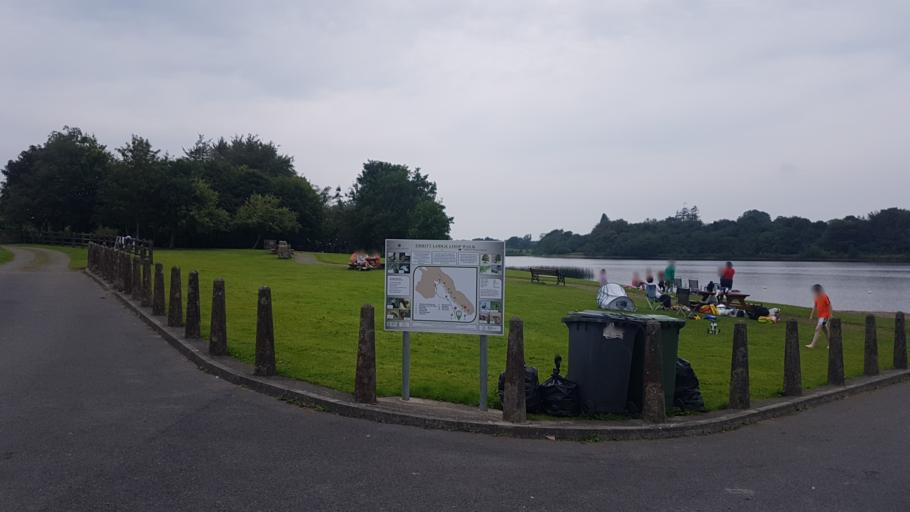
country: IE
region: Connaught
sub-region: Maigh Eo
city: Ballyhaunis
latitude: 53.8076
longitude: -8.6916
